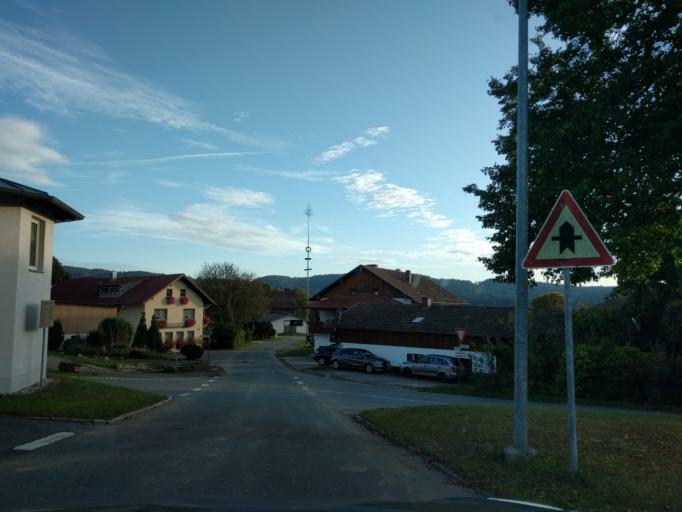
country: DE
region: Bavaria
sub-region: Upper Palatinate
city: Grafenwiesen
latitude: 49.1750
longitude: 12.8871
